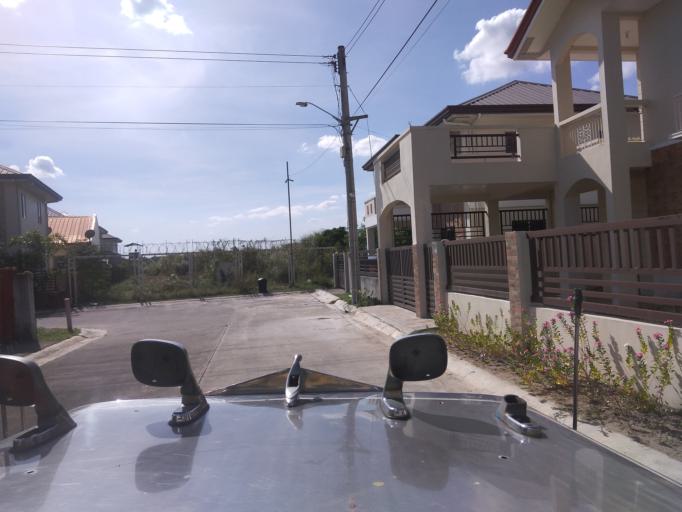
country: PH
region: Central Luzon
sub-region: Province of Pampanga
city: Magliman
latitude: 15.0249
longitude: 120.6597
